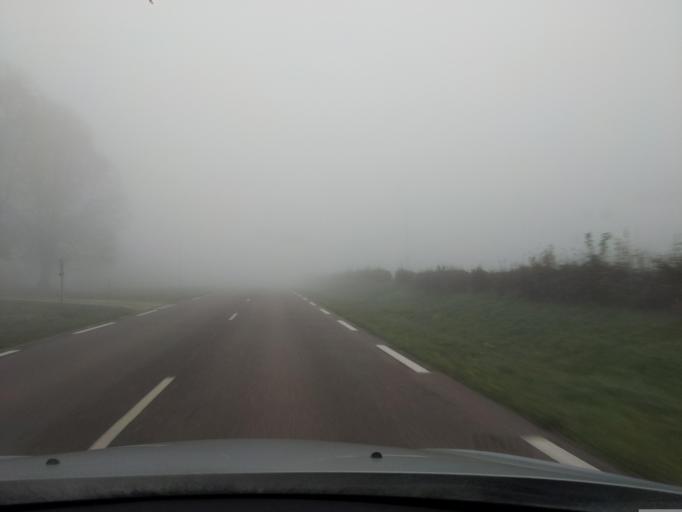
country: FR
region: Champagne-Ardenne
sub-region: Departement de la Haute-Marne
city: Langres
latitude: 47.8053
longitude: 5.2590
